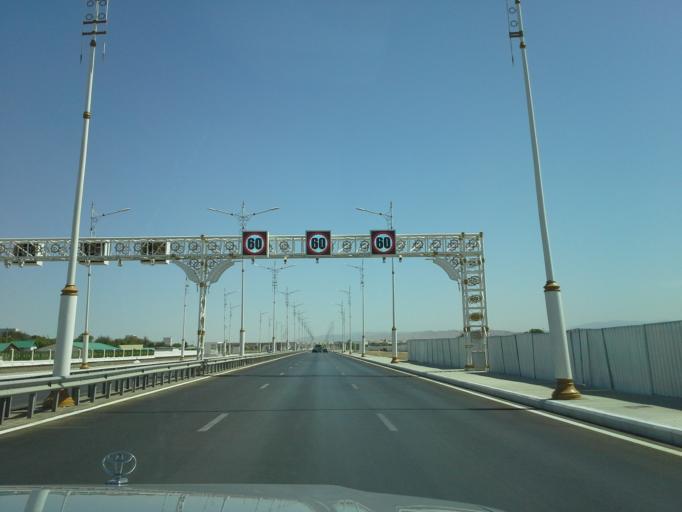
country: TM
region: Ahal
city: Ashgabat
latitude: 37.9335
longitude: 58.4135
